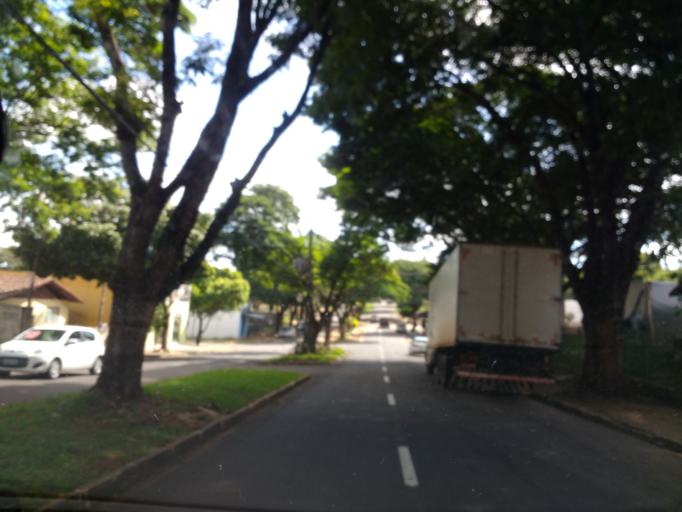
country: BR
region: Parana
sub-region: Umuarama
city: Umuarama
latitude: -23.7710
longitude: -53.3011
